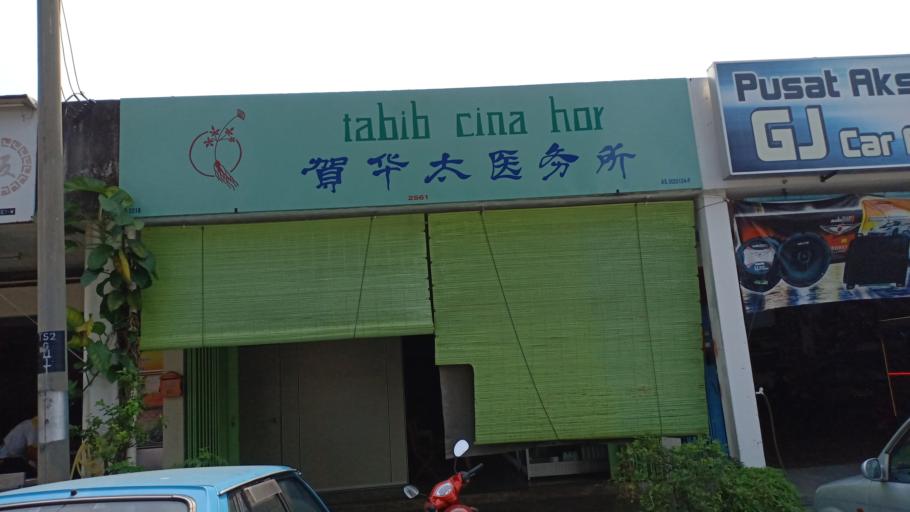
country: MY
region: Kedah
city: Kulim
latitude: 5.3777
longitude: 100.5382
